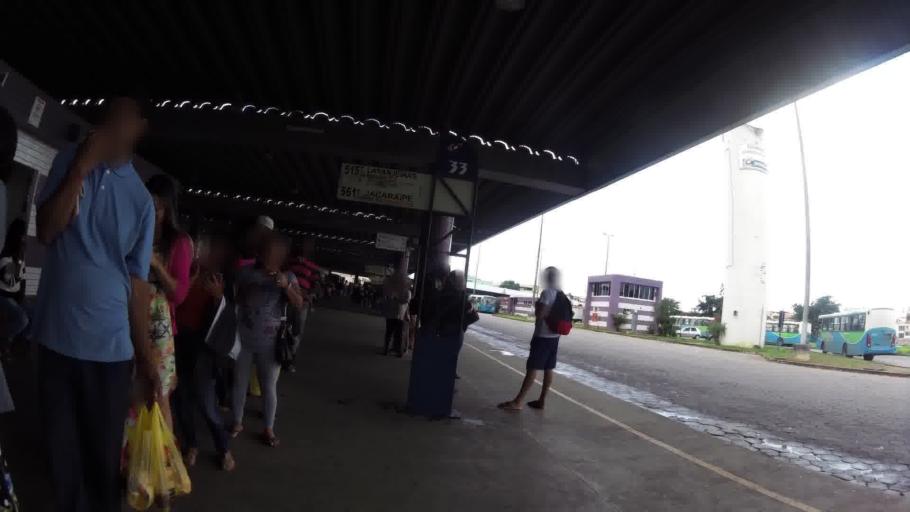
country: BR
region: Espirito Santo
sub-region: Vitoria
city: Vitoria
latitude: -20.3460
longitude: -40.3970
